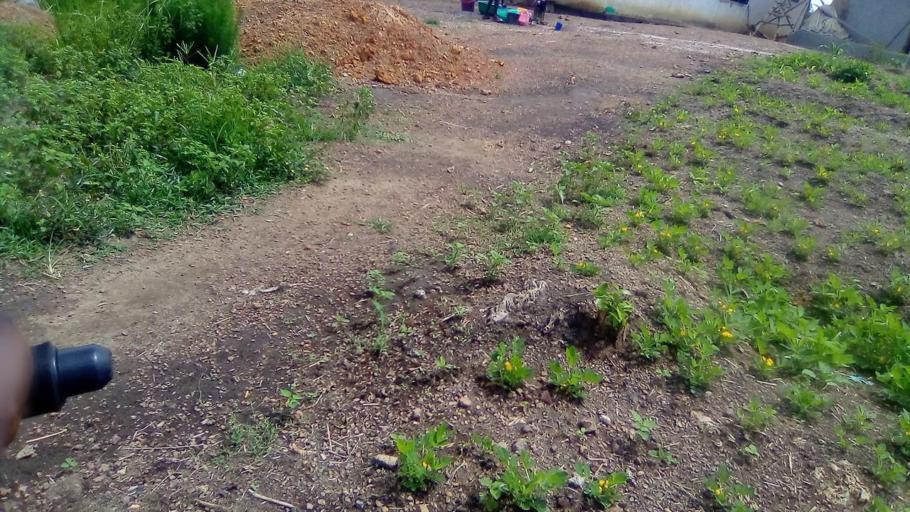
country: SL
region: Southern Province
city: Bo
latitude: 7.9358
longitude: -11.7475
